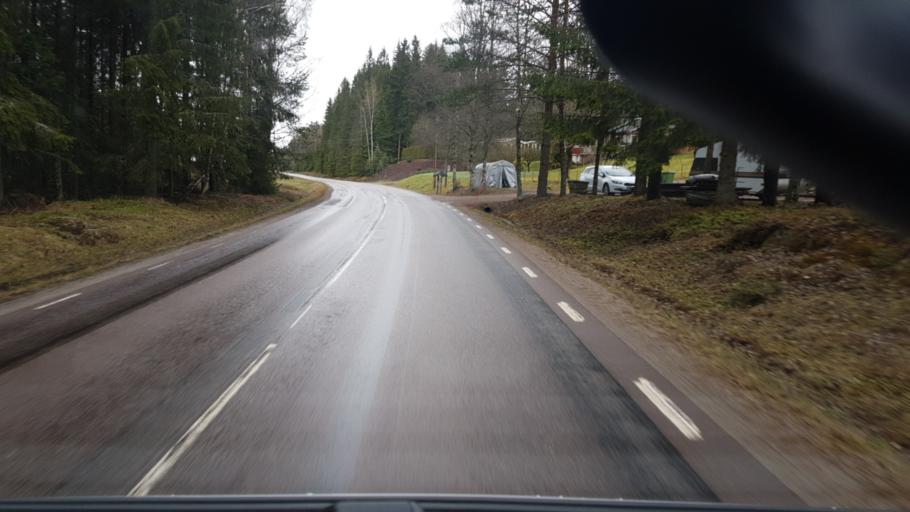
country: SE
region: Vaermland
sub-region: Eda Kommun
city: Charlottenberg
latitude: 59.8959
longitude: 12.3006
